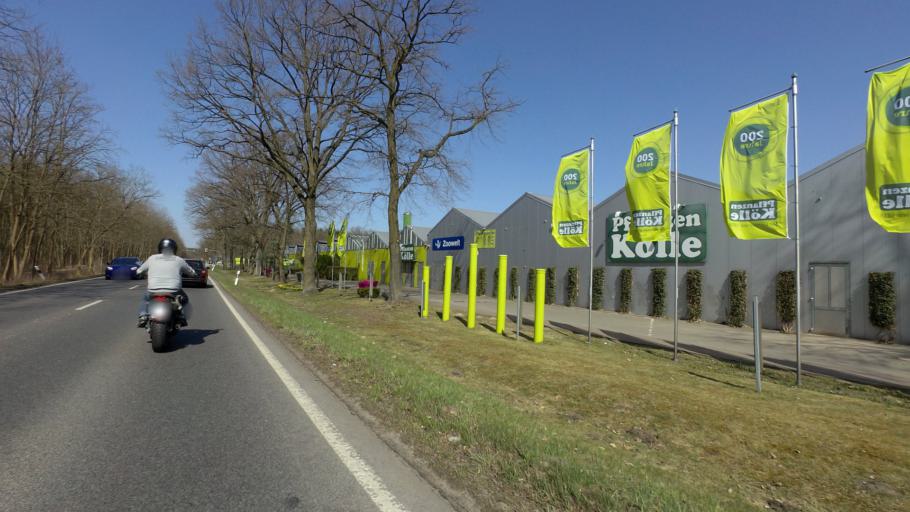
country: DE
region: Brandenburg
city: Birkenwerder
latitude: 52.7074
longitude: 13.2668
